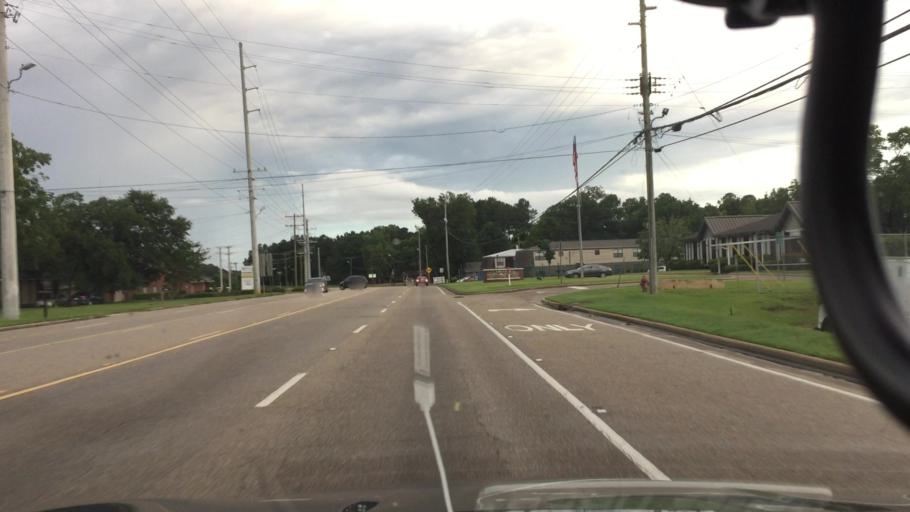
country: US
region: Alabama
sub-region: Pike County
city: Troy
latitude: 31.7835
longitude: -85.9646
